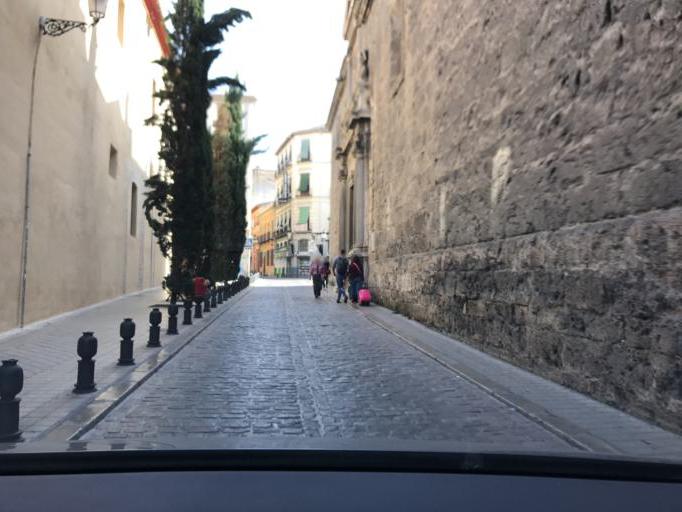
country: ES
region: Andalusia
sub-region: Provincia de Granada
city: Granada
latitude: 37.1789
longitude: -3.6017
